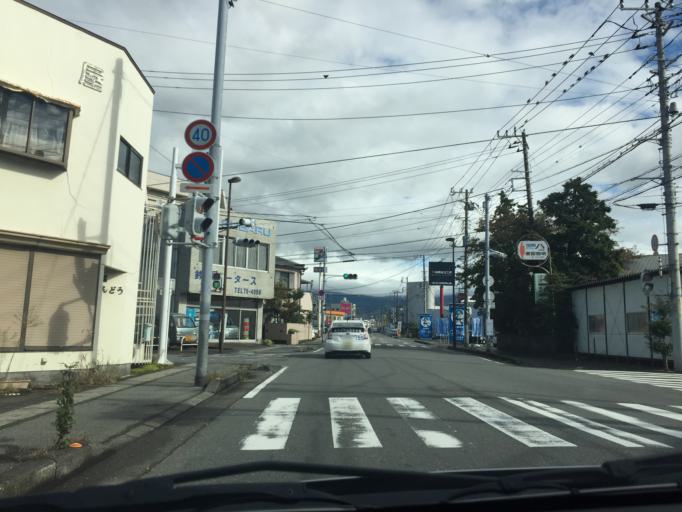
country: JP
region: Shizuoka
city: Mishima
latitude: 35.1149
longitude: 138.9003
